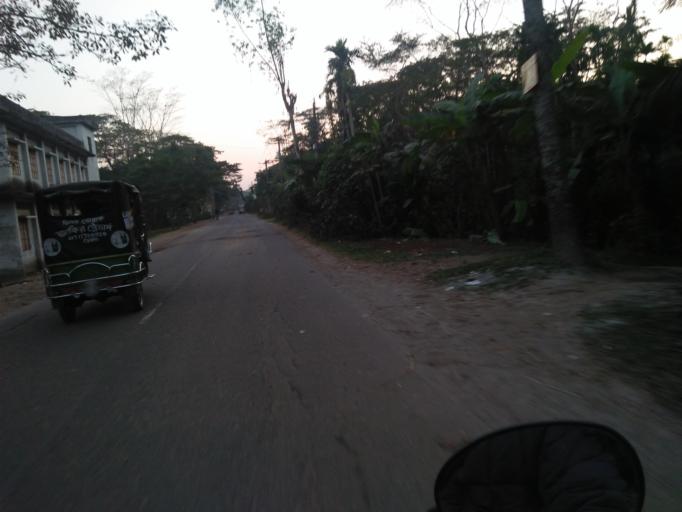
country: BD
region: Barisal
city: Bhola
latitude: 22.7566
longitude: 90.6370
